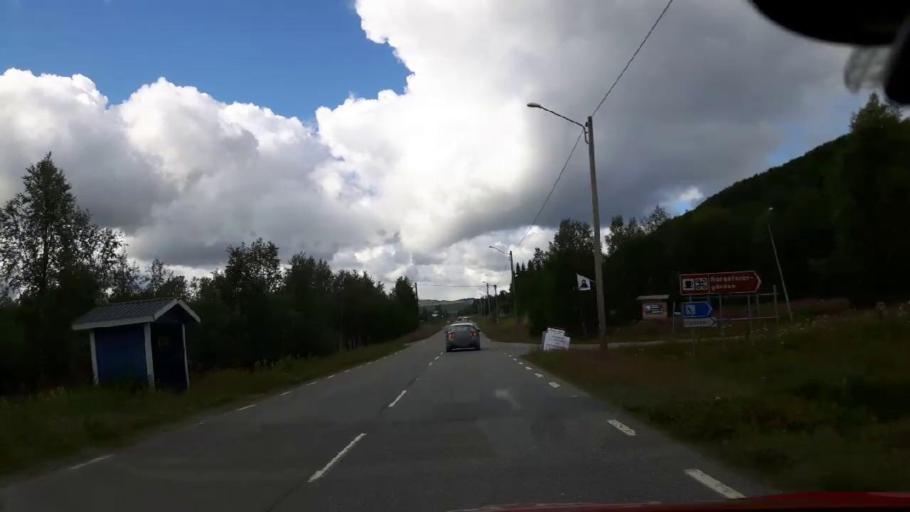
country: NO
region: Nordland
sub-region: Hattfjelldal
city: Hattfjelldal
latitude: 65.0619
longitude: 14.7996
